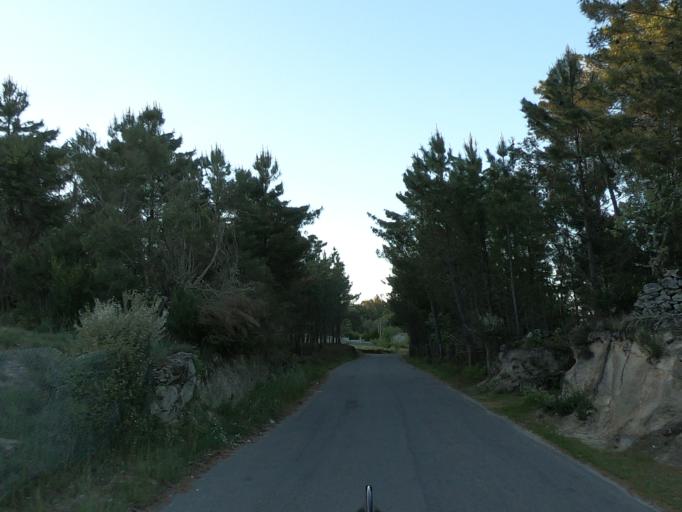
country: PT
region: Vila Real
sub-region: Sabrosa
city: Sabrosa
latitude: 41.3412
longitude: -7.6235
